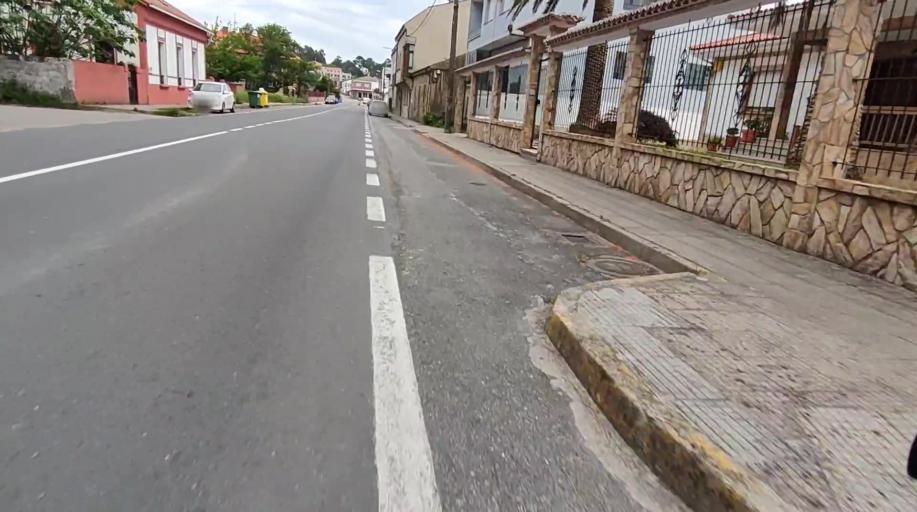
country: ES
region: Galicia
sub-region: Provincia da Coruna
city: Boiro
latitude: 42.6376
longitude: -8.8773
